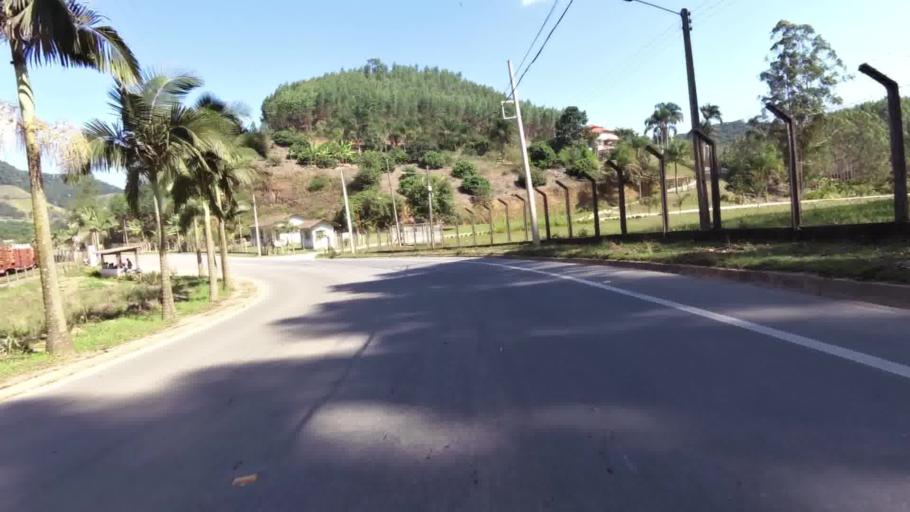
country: BR
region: Espirito Santo
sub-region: Marechal Floriano
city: Marechal Floriano
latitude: -20.4797
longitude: -40.7710
